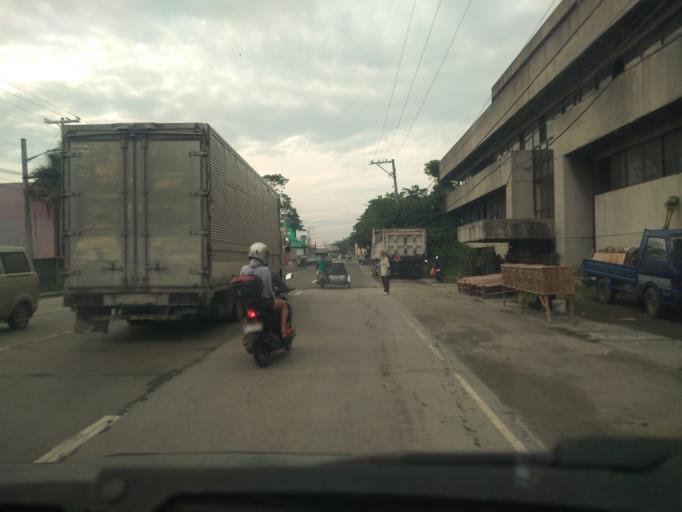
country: PH
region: Central Luzon
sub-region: Province of Pampanga
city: San Fernando
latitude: 15.0248
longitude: 120.6977
